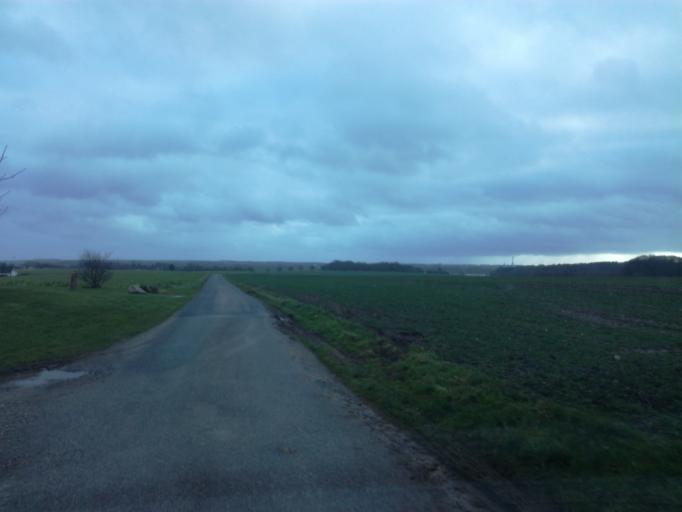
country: DK
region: South Denmark
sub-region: Vejle Kommune
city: Brejning
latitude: 55.6288
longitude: 9.6983
